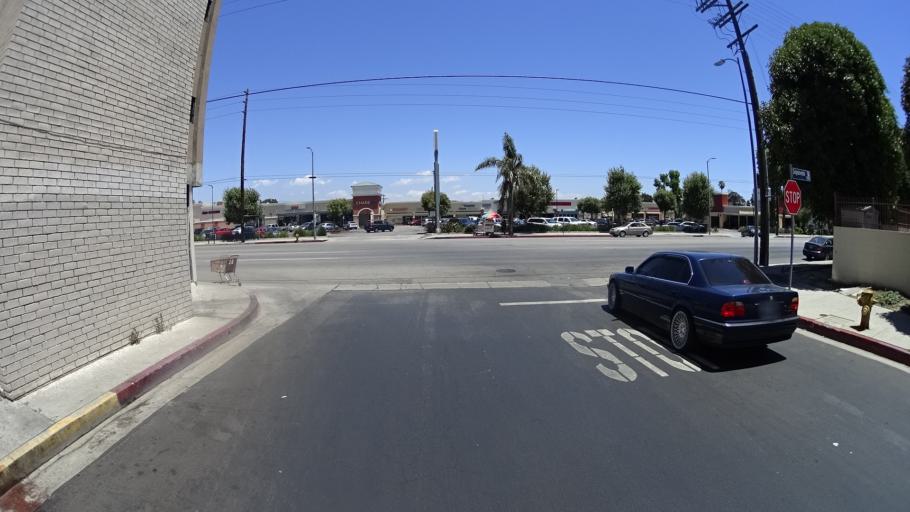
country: US
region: California
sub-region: Los Angeles County
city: Van Nuys
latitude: 34.1995
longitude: -118.4665
